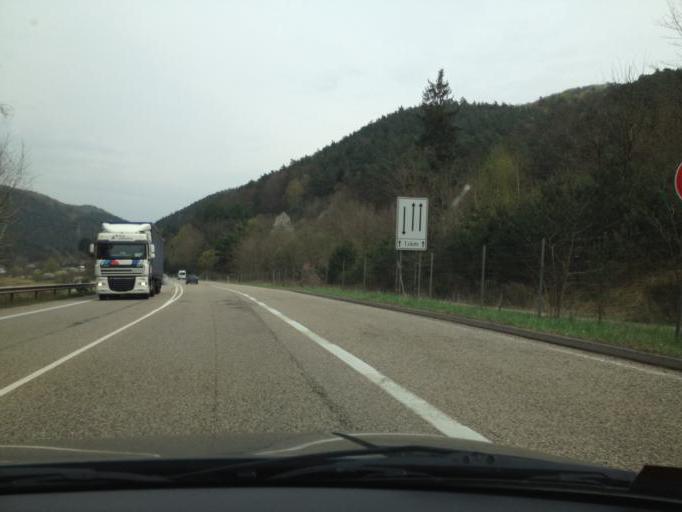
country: DE
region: Rheinland-Pfalz
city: Wilgartswiesen
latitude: 49.2150
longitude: 7.8926
